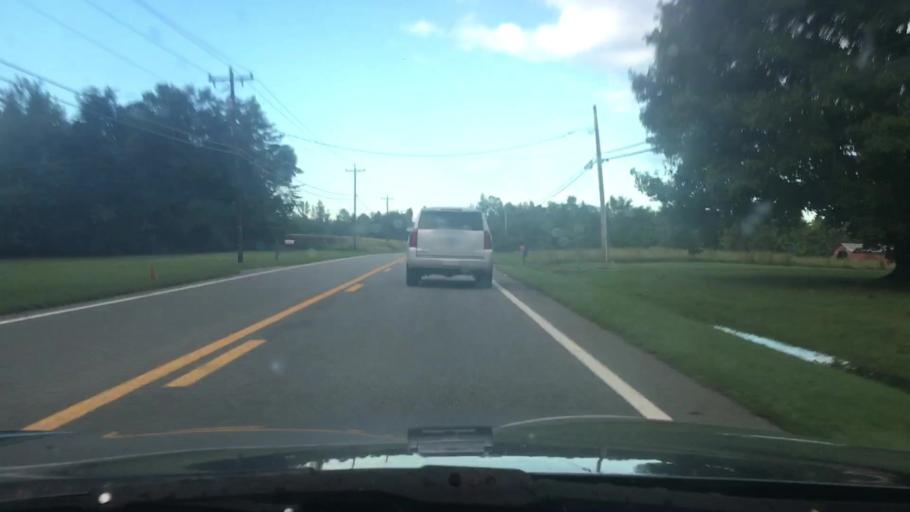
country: US
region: North Carolina
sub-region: Alamance County
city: Green Level
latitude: 36.1444
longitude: -79.3409
